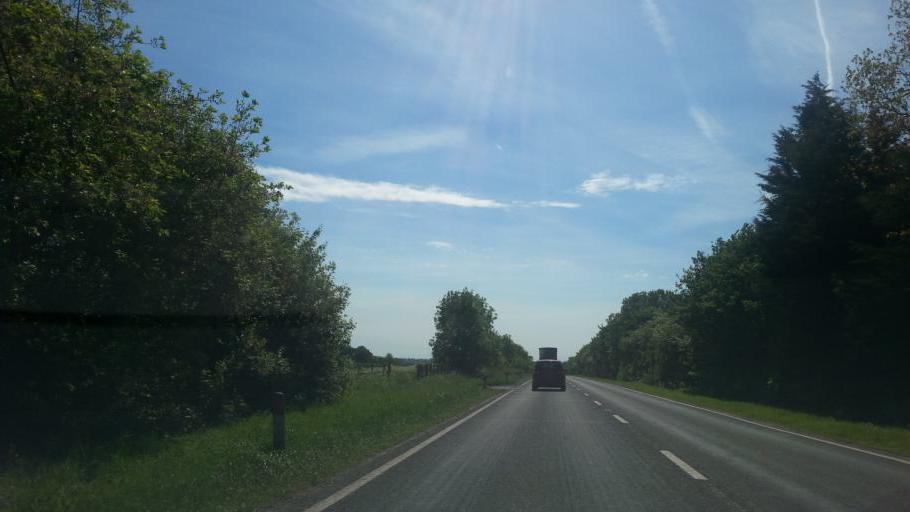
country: GB
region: England
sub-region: Cambridgeshire
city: Huntingdon
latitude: 52.3499
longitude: -0.1682
